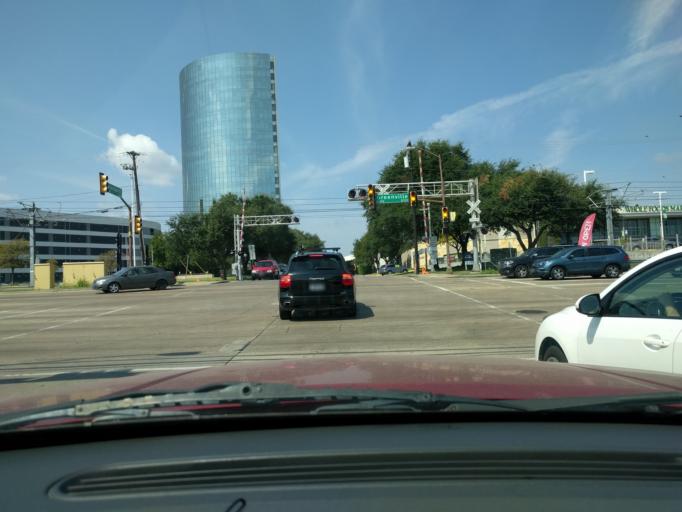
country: US
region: Texas
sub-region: Dallas County
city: University Park
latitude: 32.8671
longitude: -96.7667
